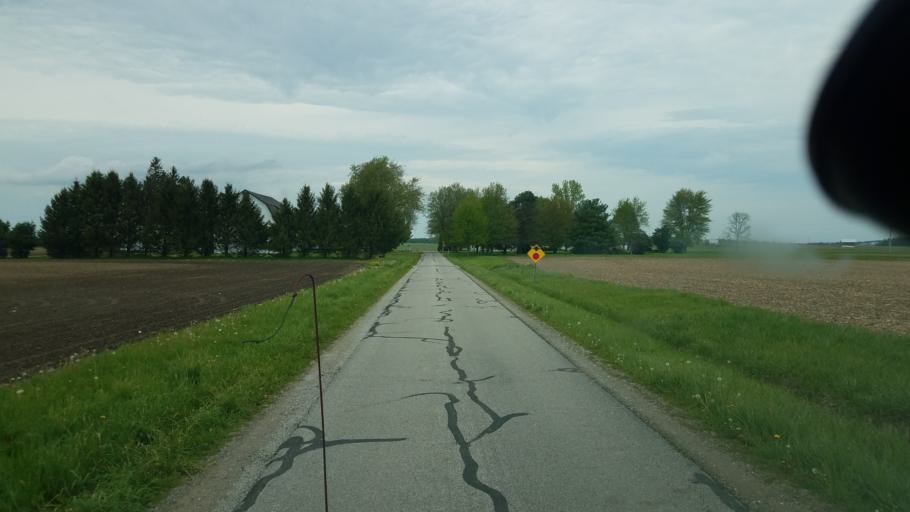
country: US
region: Ohio
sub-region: Huron County
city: Willard
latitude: 41.0423
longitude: -82.8619
